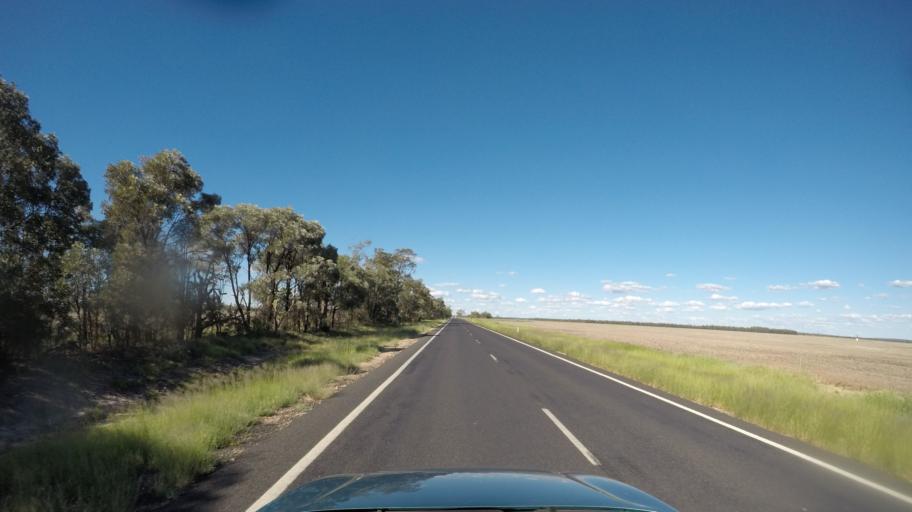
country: AU
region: Queensland
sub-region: Goondiwindi
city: Goondiwindi
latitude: -28.1459
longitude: 150.6864
